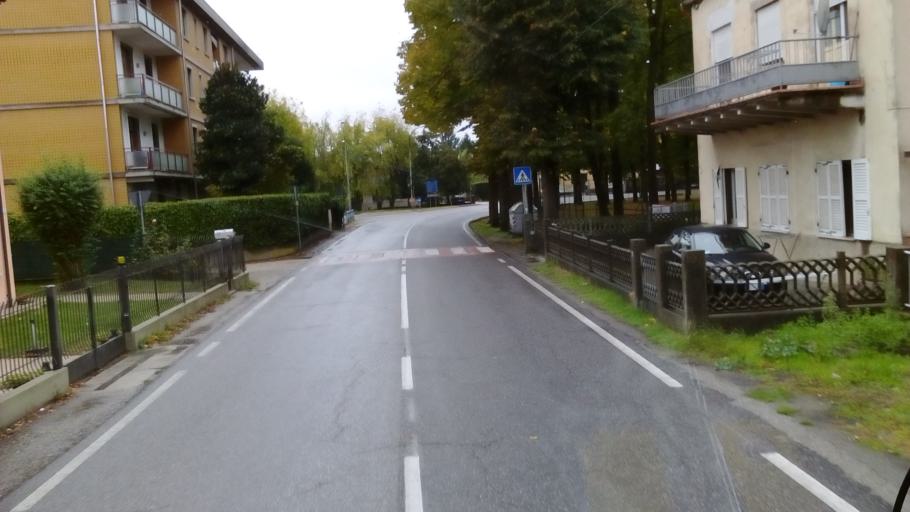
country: IT
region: Emilia-Romagna
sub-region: Provincia di Reggio Emilia
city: Luzzara
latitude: 44.9599
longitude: 10.6882
